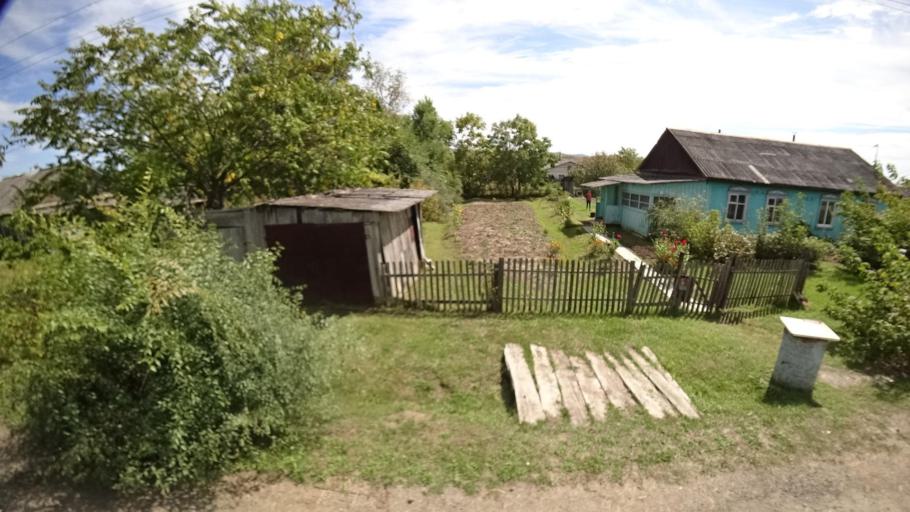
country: RU
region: Primorskiy
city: Yakovlevka
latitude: 44.6444
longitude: 133.5922
